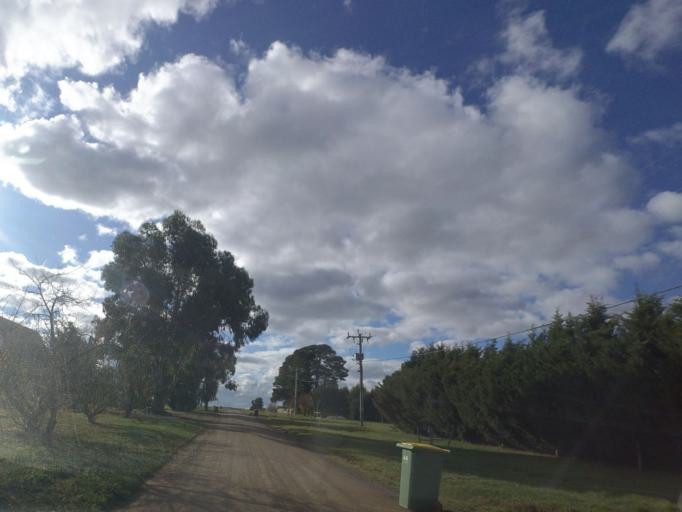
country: AU
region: Victoria
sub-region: Mount Alexander
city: Castlemaine
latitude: -37.1865
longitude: 144.3910
